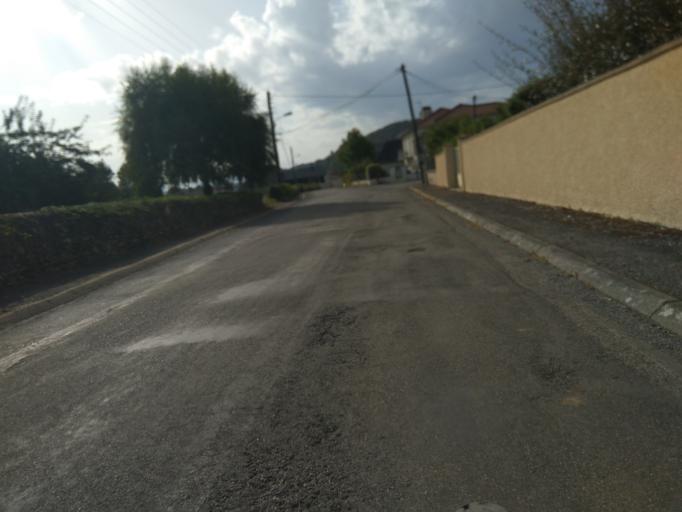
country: FR
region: Aquitaine
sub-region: Departement des Pyrenees-Atlantiques
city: Mazeres-Lezons
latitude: 43.2681
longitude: -0.3425
